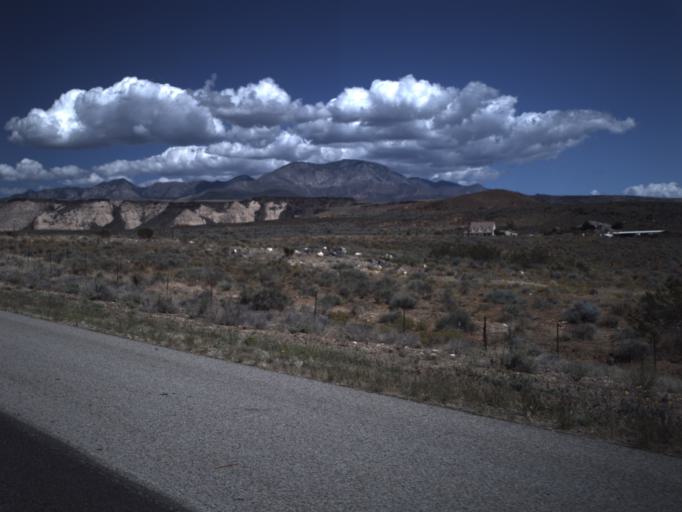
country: US
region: Utah
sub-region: Washington County
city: Santa Clara
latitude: 37.1775
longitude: -113.6188
